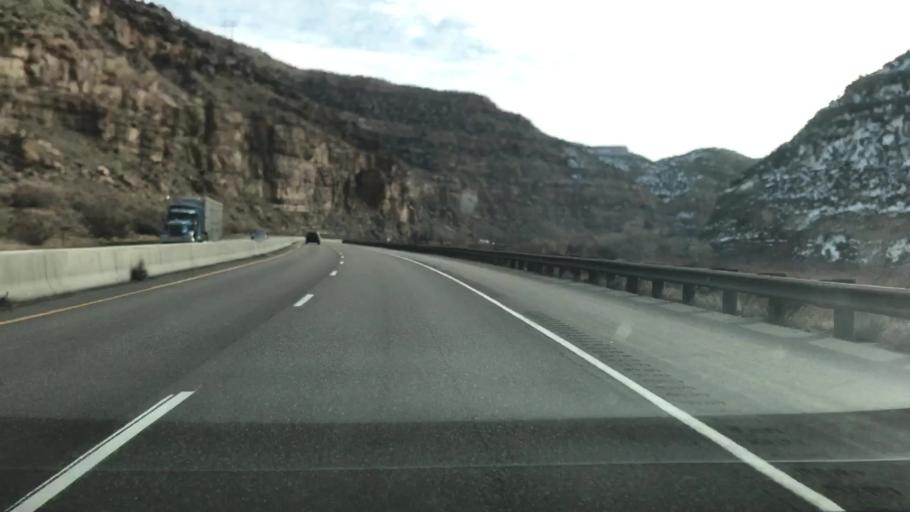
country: US
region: Colorado
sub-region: Mesa County
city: Palisade
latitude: 39.2303
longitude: -108.2694
